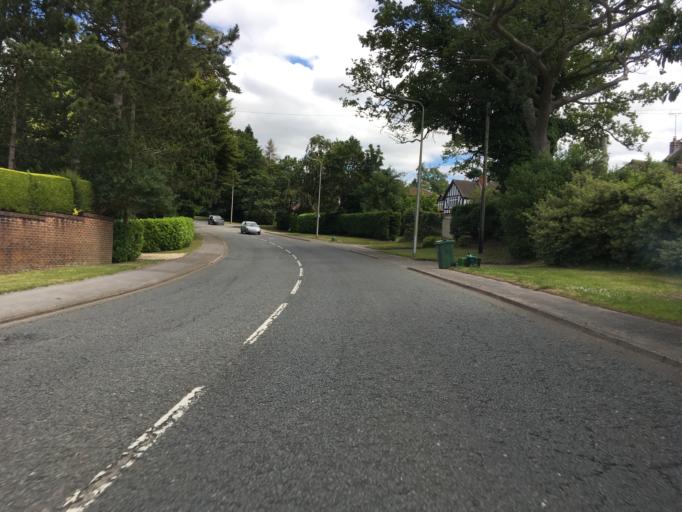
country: GB
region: England
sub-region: West Berkshire
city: Newbury
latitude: 51.3709
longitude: -1.3475
